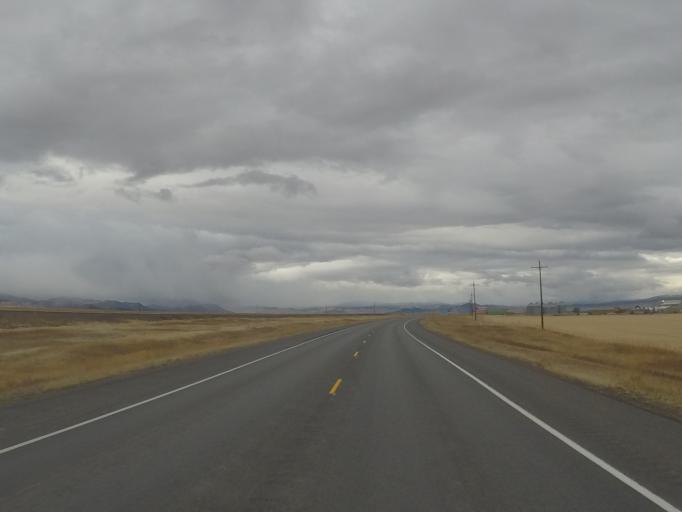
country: US
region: Montana
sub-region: Lewis and Clark County
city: East Helena
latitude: 46.5712
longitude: -111.8232
